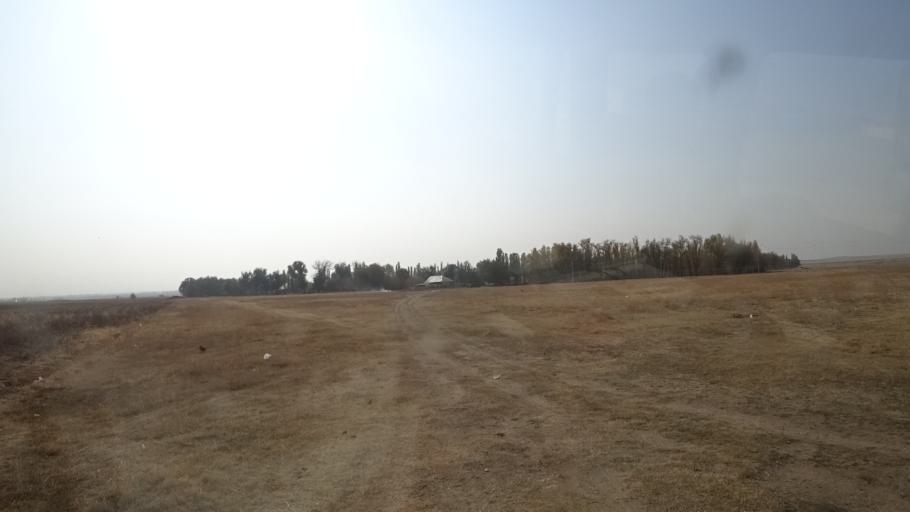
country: KZ
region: Zhambyl
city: Sarykemer
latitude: 43.0780
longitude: 71.6171
